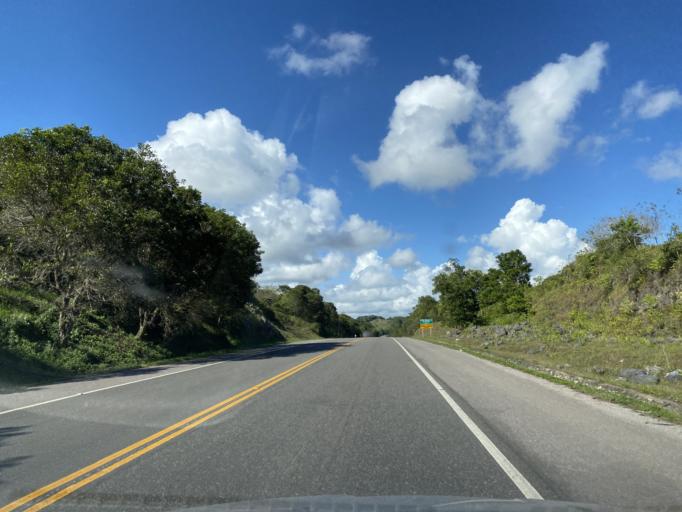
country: DO
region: Monte Plata
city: Majagual
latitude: 19.0264
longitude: -69.8234
